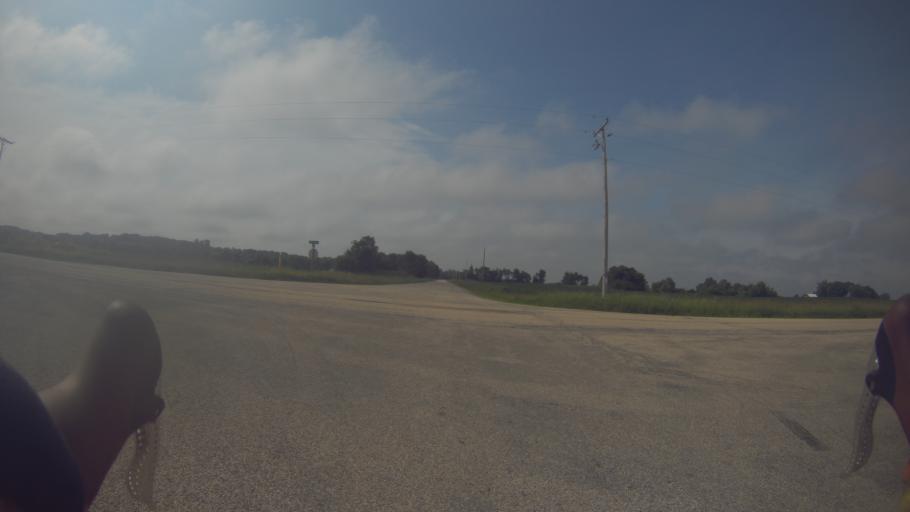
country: US
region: Wisconsin
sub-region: Dane County
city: Stoughton
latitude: 42.9413
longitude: -89.1811
